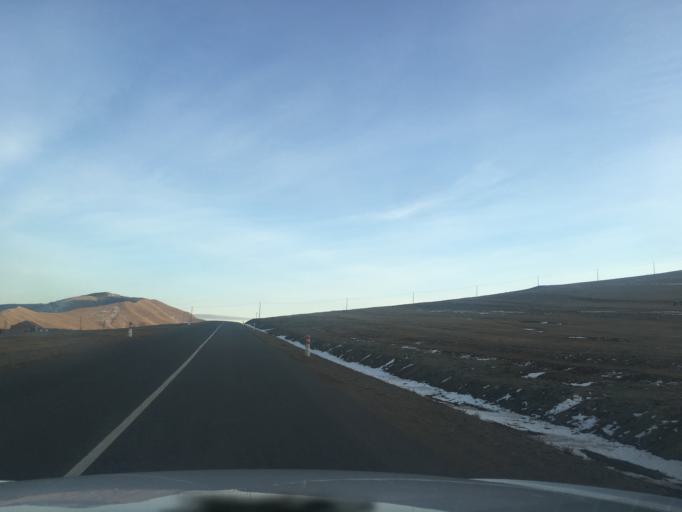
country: MN
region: Central Aimak
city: Mandal
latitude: 48.1985
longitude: 106.7060
